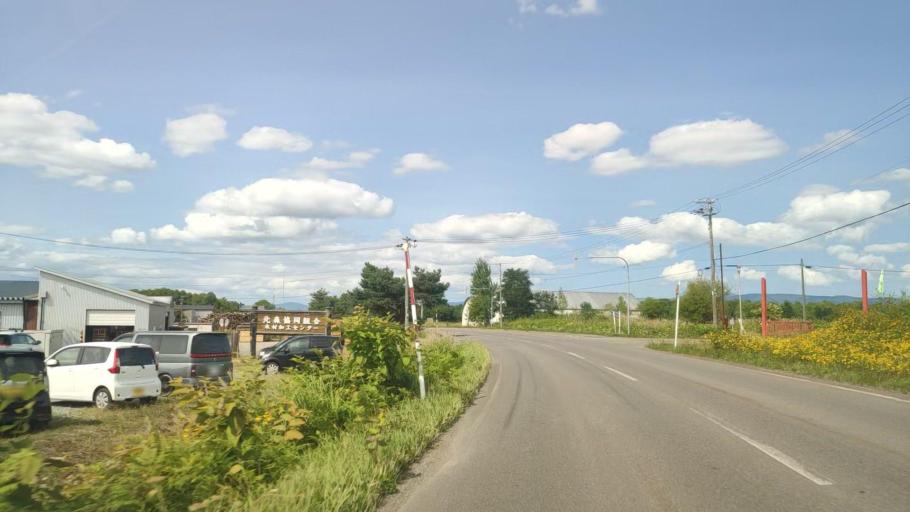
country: JP
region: Hokkaido
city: Nayoro
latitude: 44.2833
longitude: 142.4292
